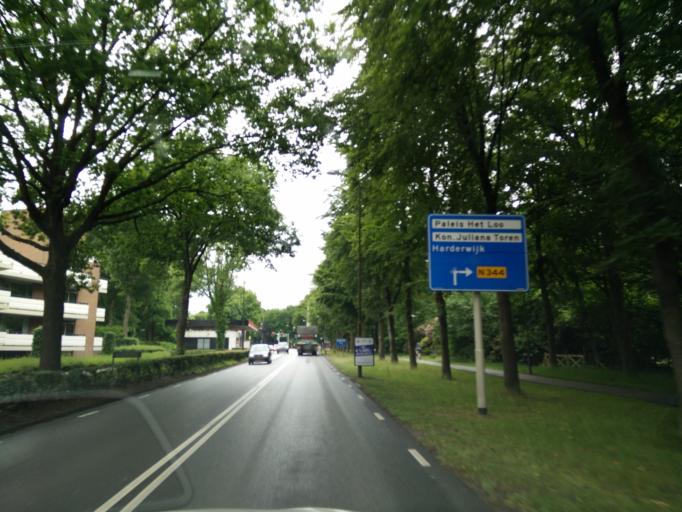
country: NL
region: Gelderland
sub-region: Gemeente Apeldoorn
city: Apeldoorn
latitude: 52.2289
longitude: 5.9485
